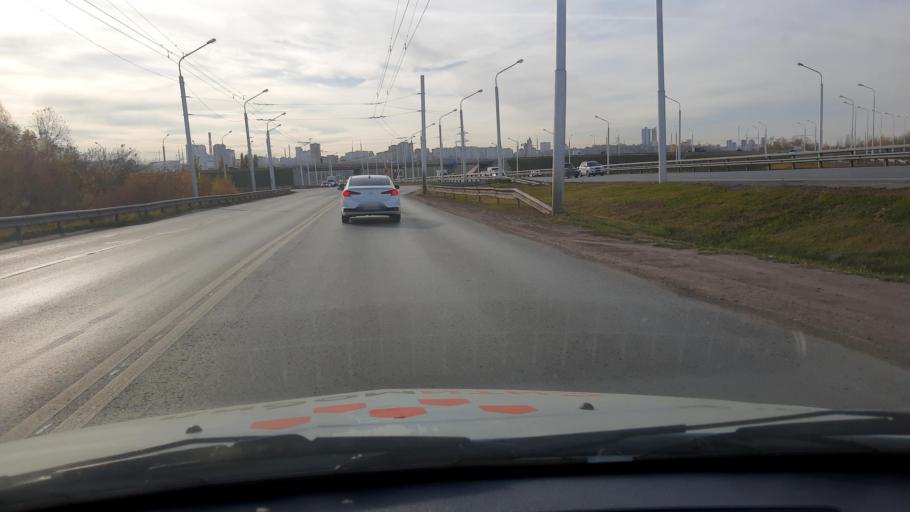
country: RU
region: Bashkortostan
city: Ufa
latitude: 54.7677
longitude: 55.9551
